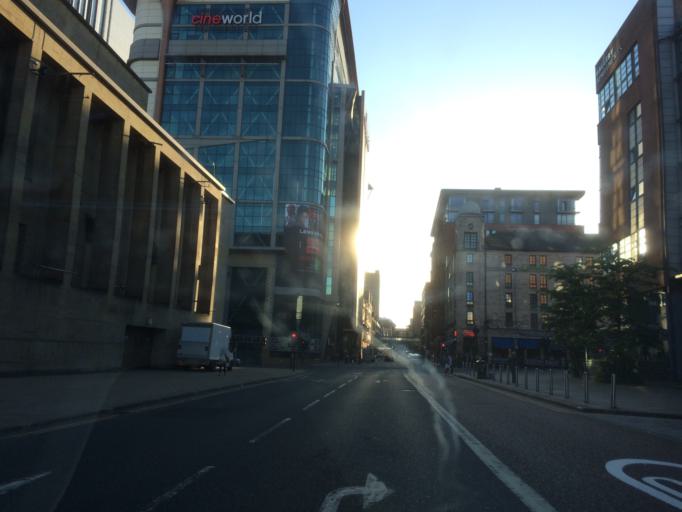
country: GB
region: Scotland
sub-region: Glasgow City
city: Glasgow
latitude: 55.8649
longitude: -4.2527
